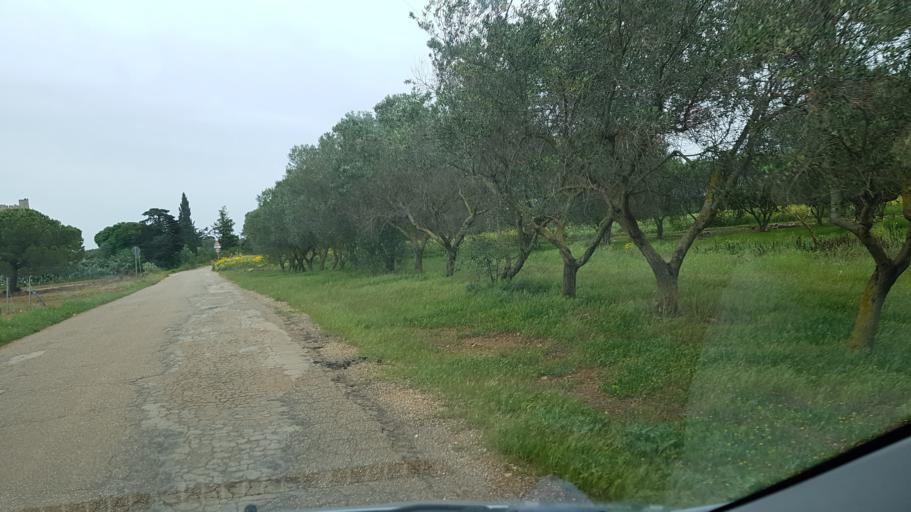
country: IT
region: Apulia
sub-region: Provincia di Brindisi
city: San Vito dei Normanni
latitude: 40.6209
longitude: 17.7559
